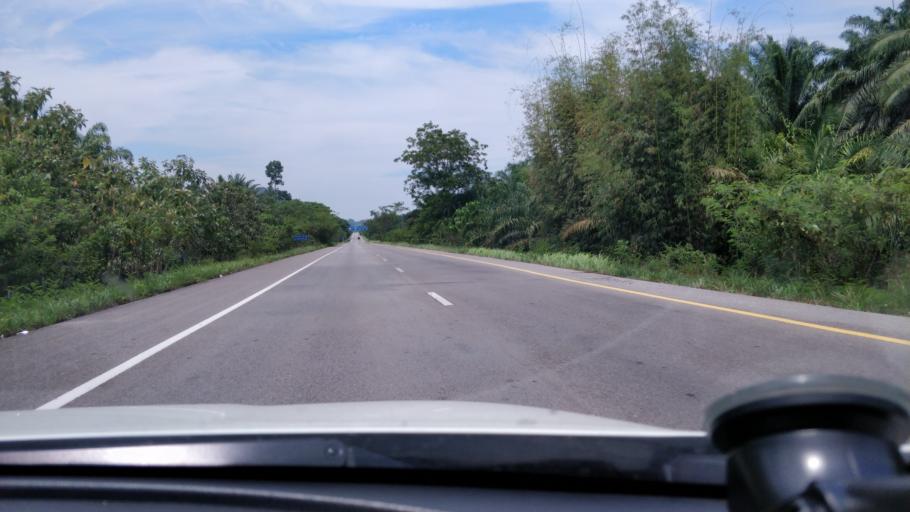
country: TH
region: Krabi
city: Plai Phraya
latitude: 8.5680
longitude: 98.9250
